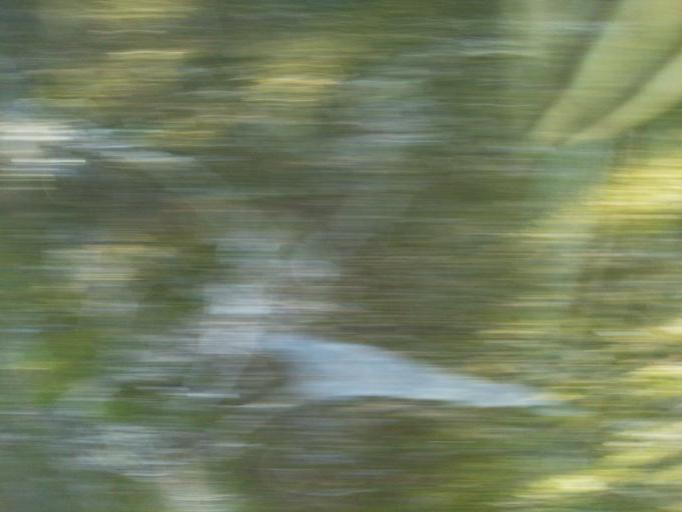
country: JP
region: Kochi
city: Nakamura
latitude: 33.1160
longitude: 133.1128
